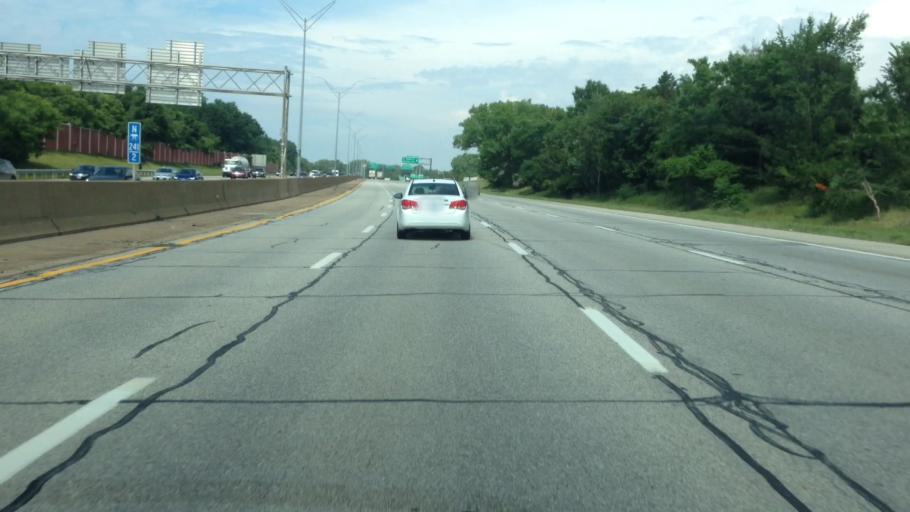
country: US
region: Ohio
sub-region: Cuyahoga County
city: Lakewood
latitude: 41.4398
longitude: -81.7889
